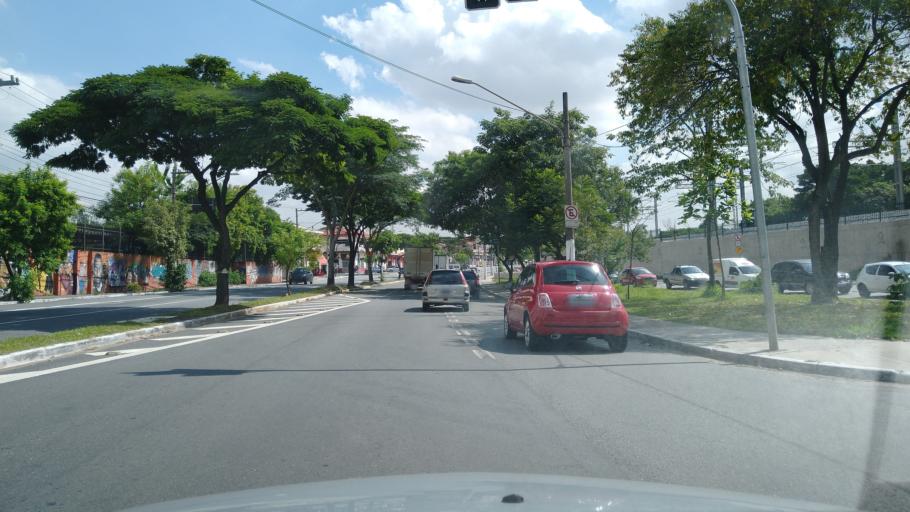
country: BR
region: Sao Paulo
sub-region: Guarulhos
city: Guarulhos
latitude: -23.4997
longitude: -46.5232
